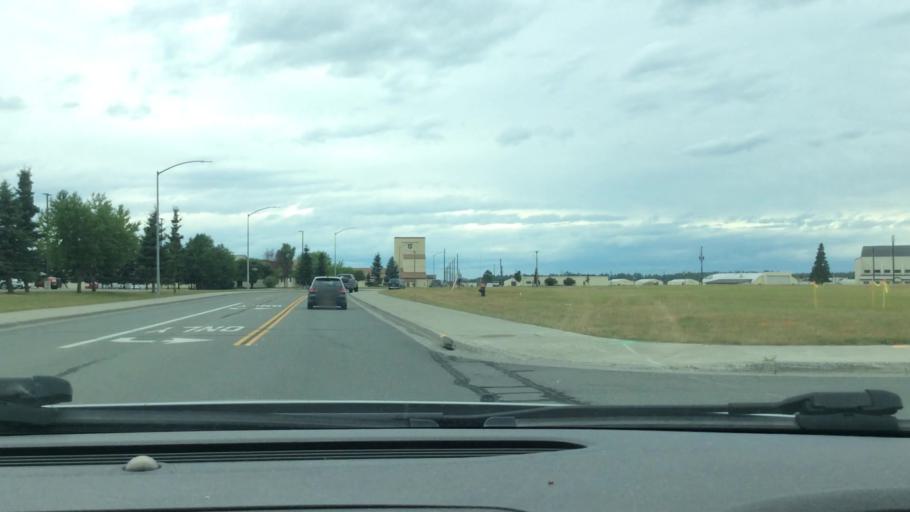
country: US
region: Alaska
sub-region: Anchorage Municipality
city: Anchorage
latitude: 61.2374
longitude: -149.8265
